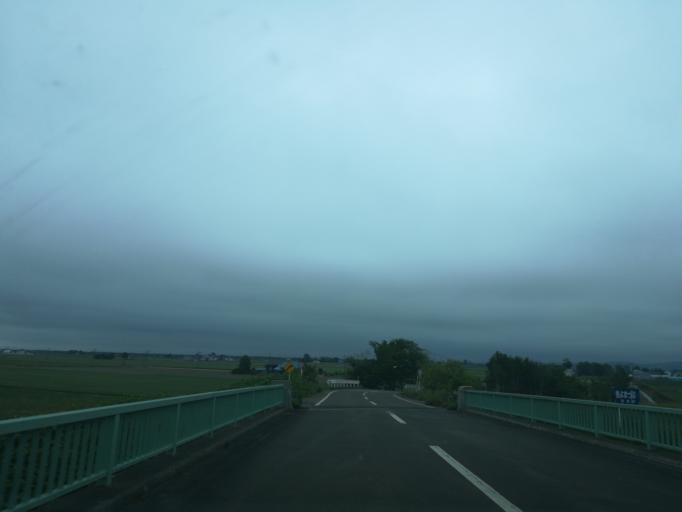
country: JP
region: Hokkaido
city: Iwamizawa
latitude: 43.1298
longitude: 141.6982
